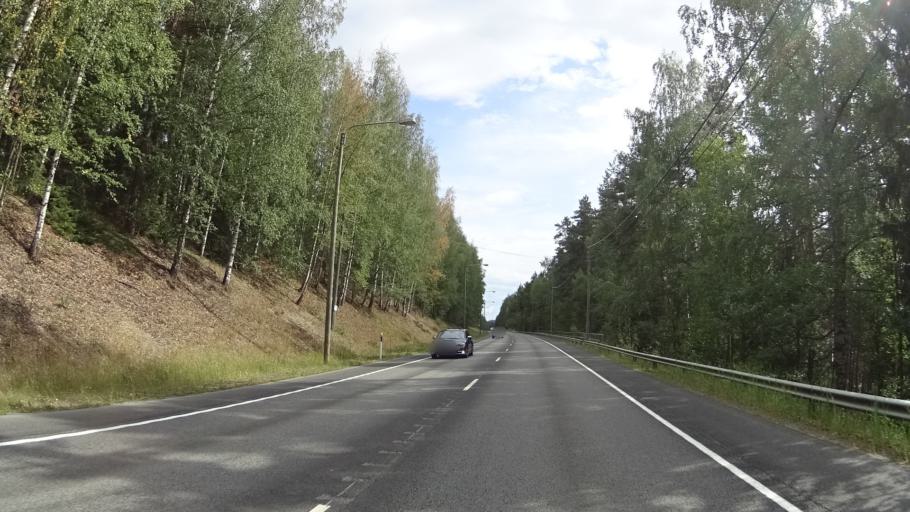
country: FI
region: Pirkanmaa
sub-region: Tampere
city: Kangasala
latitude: 61.4309
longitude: 24.1290
